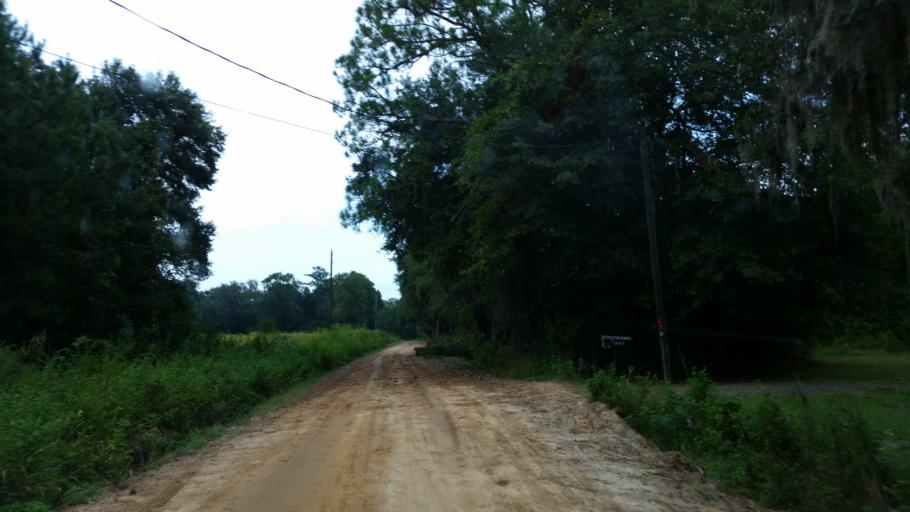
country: US
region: Georgia
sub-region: Lowndes County
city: Valdosta
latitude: 30.7206
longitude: -83.2891
